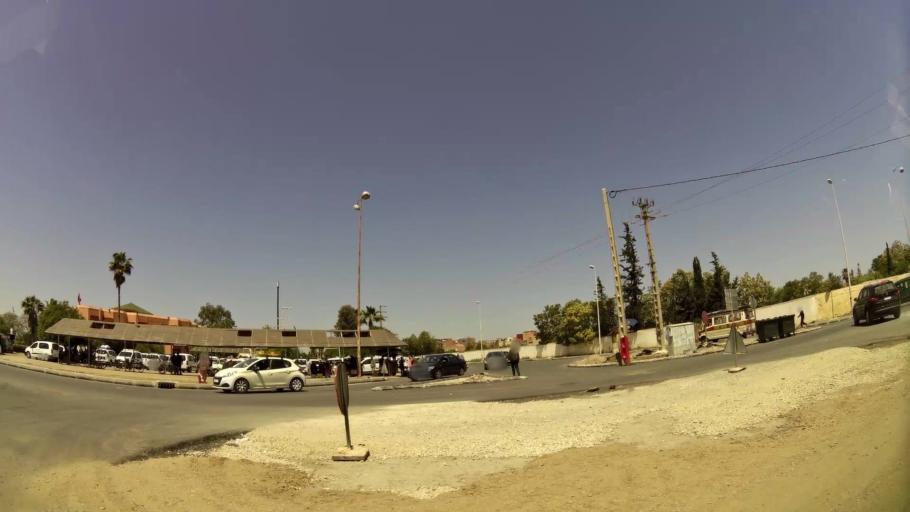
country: MA
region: Rabat-Sale-Zemmour-Zaer
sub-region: Khemisset
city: Khemisset
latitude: 33.8211
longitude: -6.0723
